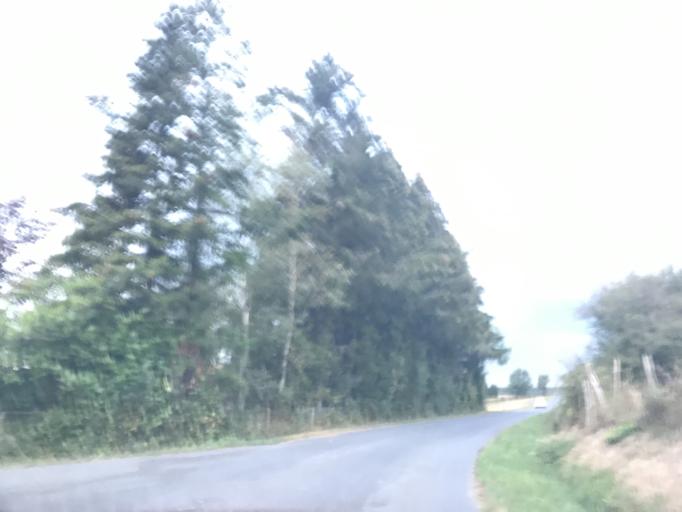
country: FR
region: Auvergne
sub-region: Departement du Puy-de-Dome
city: Escoutoux
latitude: 45.7869
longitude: 3.5813
